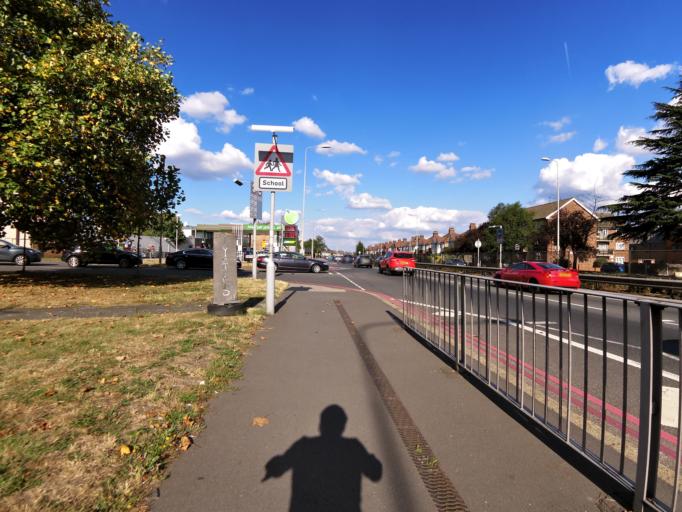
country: GB
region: England
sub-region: Greater London
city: Wood Green
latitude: 51.6146
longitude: -0.1018
